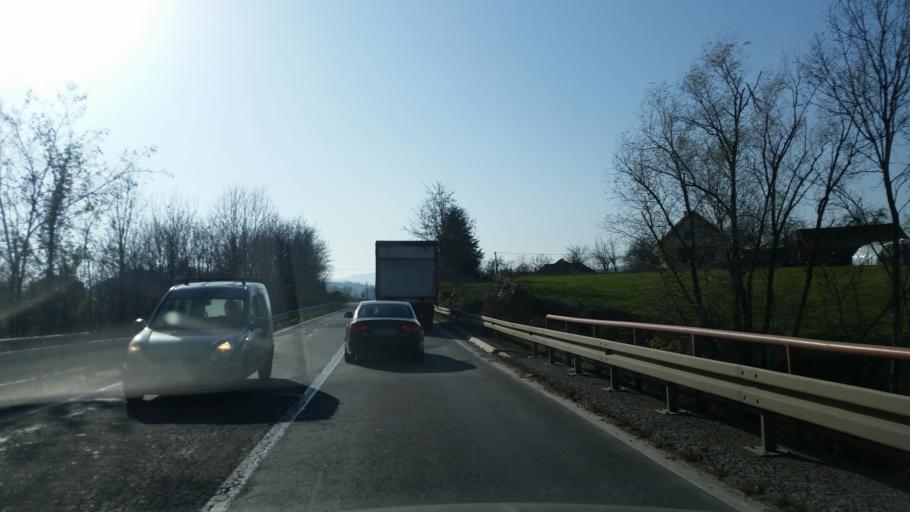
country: RS
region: Central Serbia
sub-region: Kolubarski Okrug
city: Ljig
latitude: 44.2525
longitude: 20.2856
